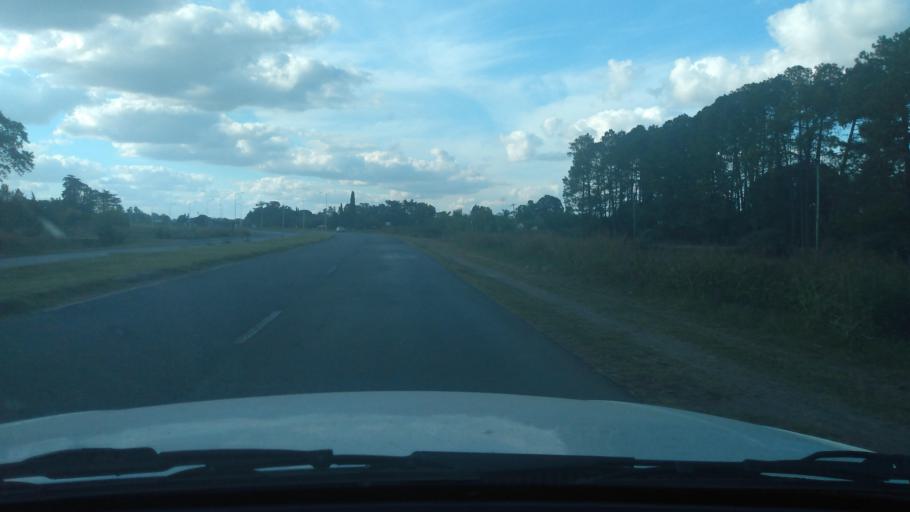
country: AR
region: Buenos Aires
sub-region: Partido de Mercedes
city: Mercedes
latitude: -34.6721
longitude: -59.3995
